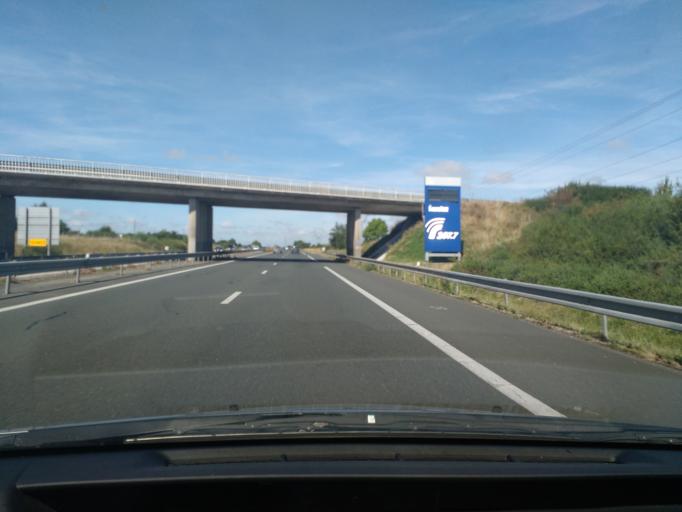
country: FR
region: Pays de la Loire
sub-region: Departement de la Loire-Atlantique
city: Varades
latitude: 47.4211
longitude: -1.0285
